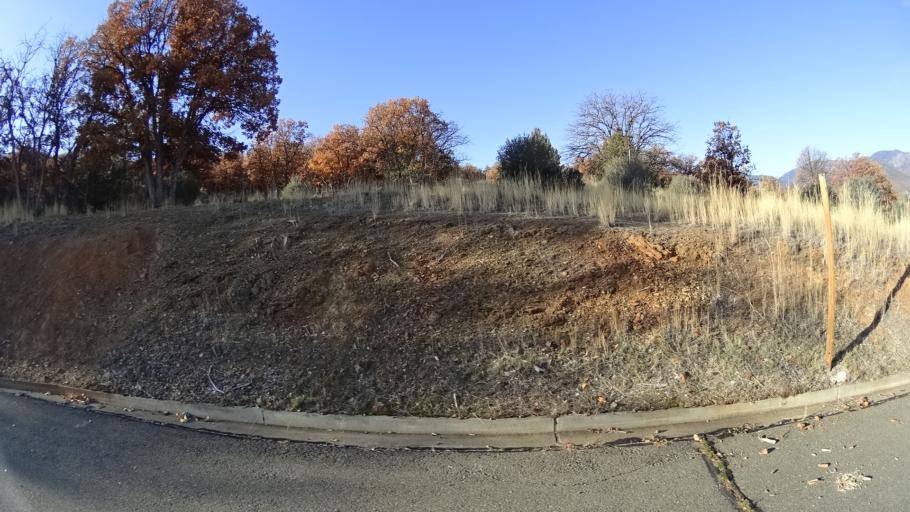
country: US
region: California
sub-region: Siskiyou County
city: Yreka
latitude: 41.7137
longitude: -122.6279
